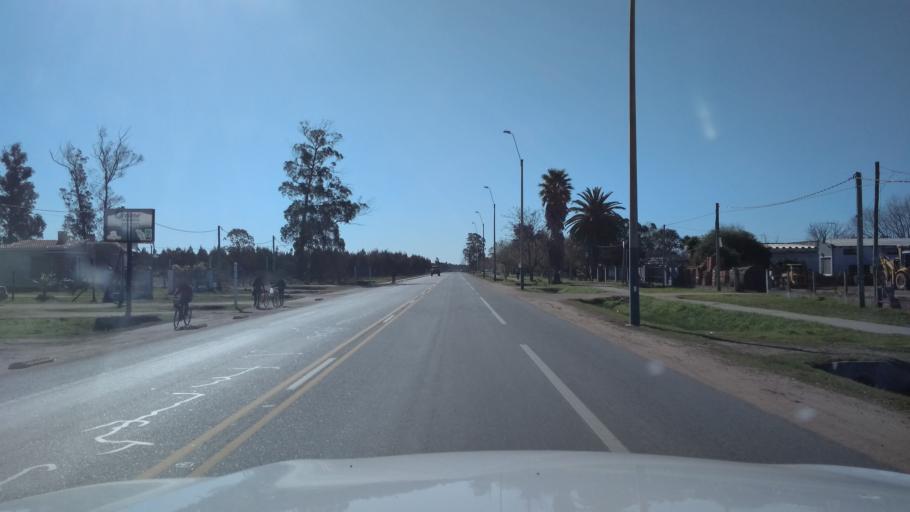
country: UY
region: Canelones
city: Atlantida
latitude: -34.7534
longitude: -55.7675
